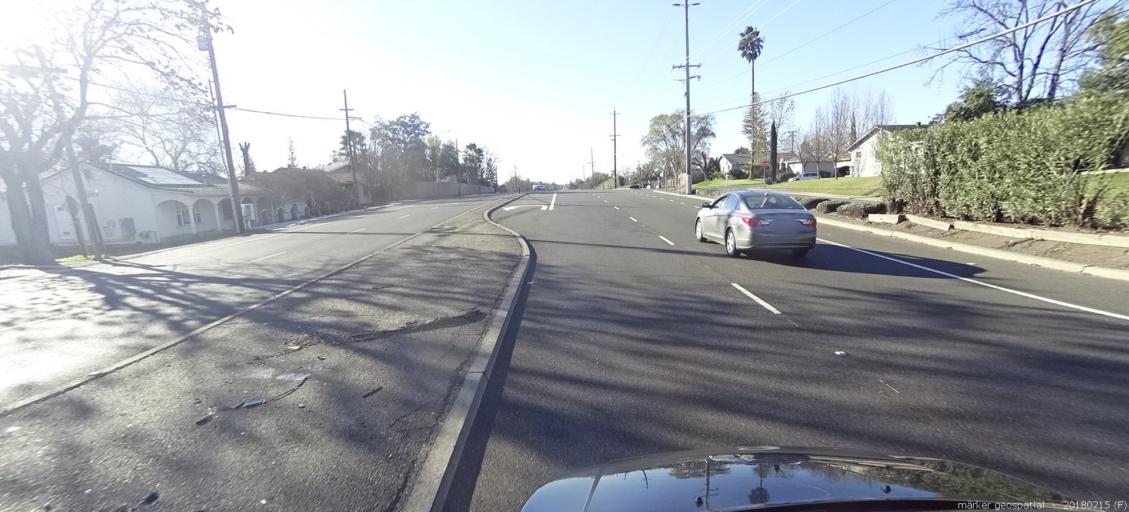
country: US
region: California
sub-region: Sacramento County
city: Foothill Farms
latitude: 38.6751
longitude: -121.3367
